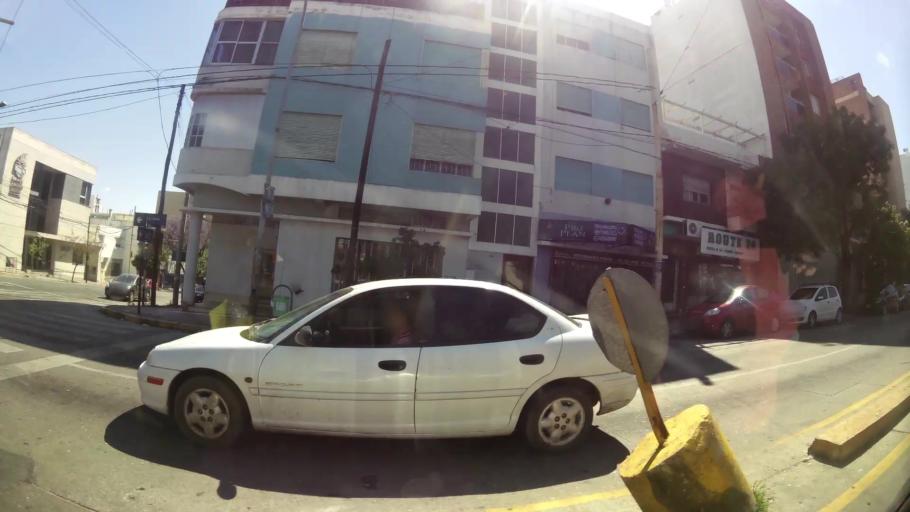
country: AR
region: Cordoba
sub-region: Departamento de Capital
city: Cordoba
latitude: -31.4110
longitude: -64.1572
